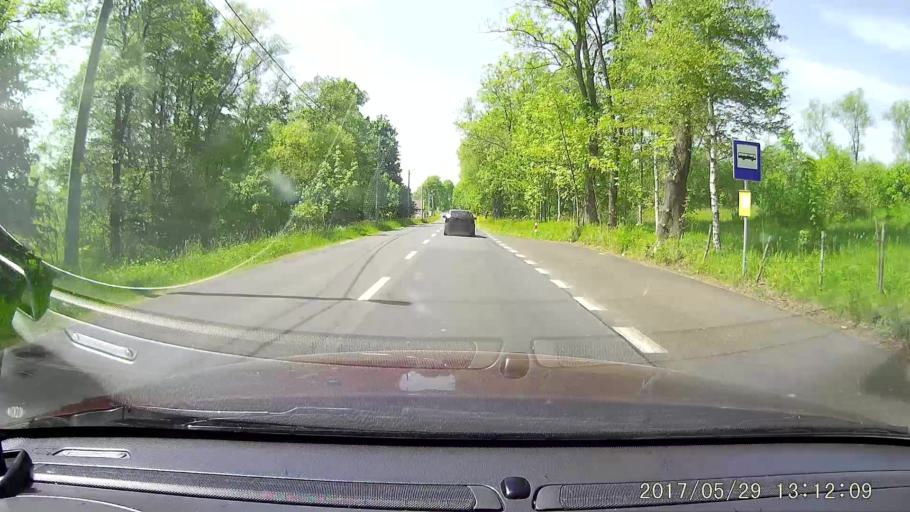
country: PL
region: Lower Silesian Voivodeship
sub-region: Powiat lwowecki
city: Lubomierz
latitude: 50.9671
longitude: 15.5102
